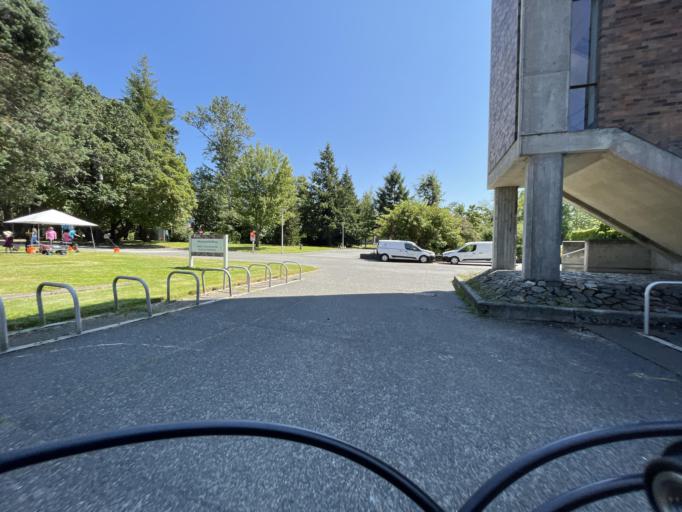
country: CA
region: British Columbia
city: Oak Bay
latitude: 48.4629
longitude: -123.3133
